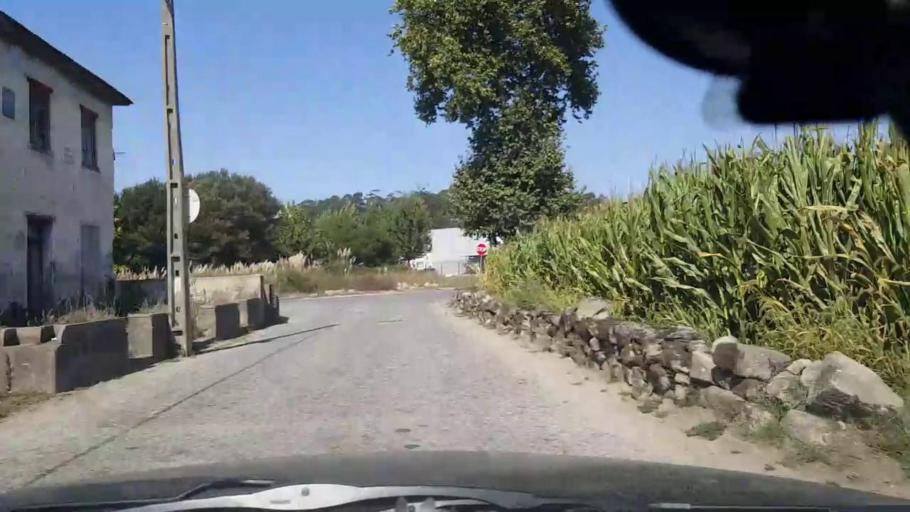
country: PT
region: Porto
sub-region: Vila do Conde
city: Vila do Conde
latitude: 41.3645
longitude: -8.7271
